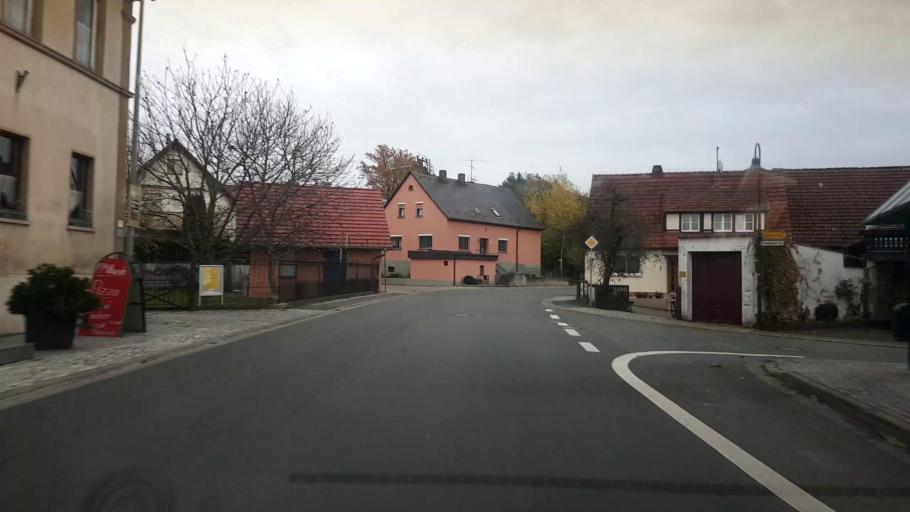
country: DE
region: Bavaria
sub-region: Regierungsbezirk Unterfranken
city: Wiesentheid
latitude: 49.7943
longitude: 10.3551
